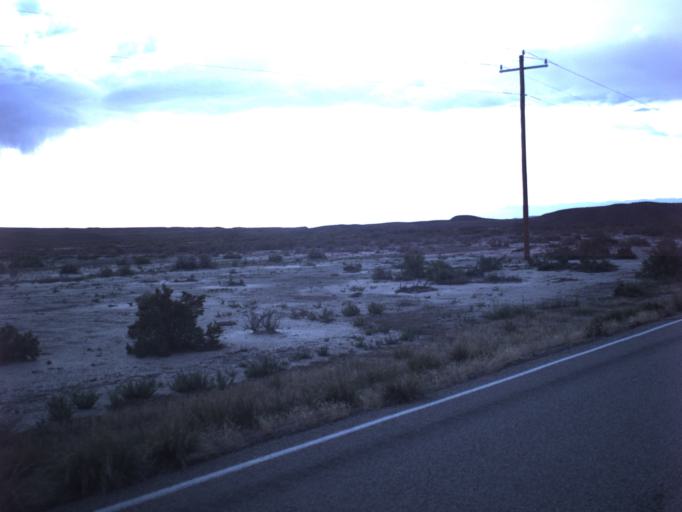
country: US
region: Utah
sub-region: Grand County
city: Moab
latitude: 38.8772
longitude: -109.3079
